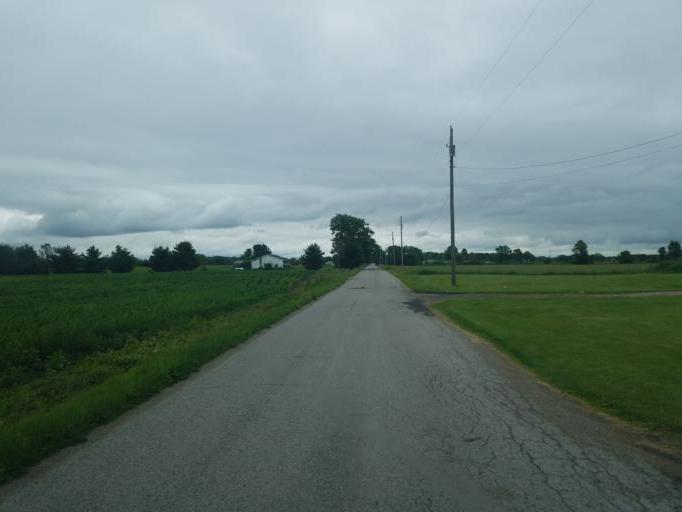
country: US
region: Ohio
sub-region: Morrow County
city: Cardington
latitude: 40.5280
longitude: -82.8900
